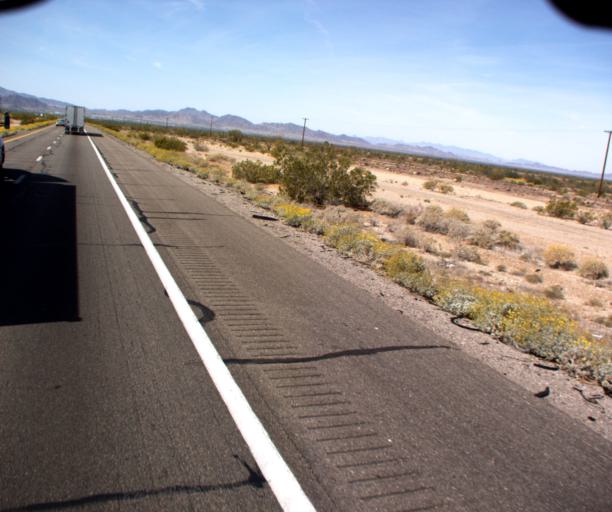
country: US
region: Arizona
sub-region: La Paz County
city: Quartzsite
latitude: 33.6772
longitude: -114.1194
